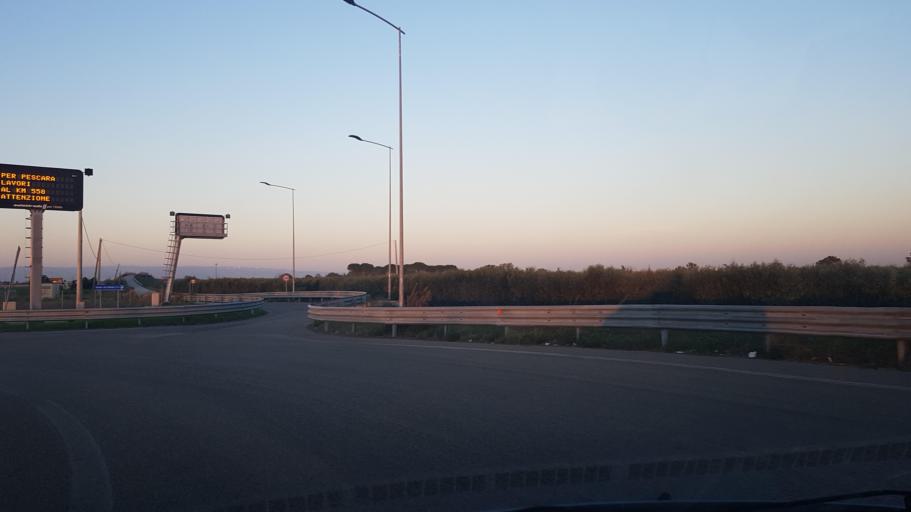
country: IT
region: Apulia
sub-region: Provincia di Foggia
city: Carapelle
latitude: 41.4208
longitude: 15.6565
